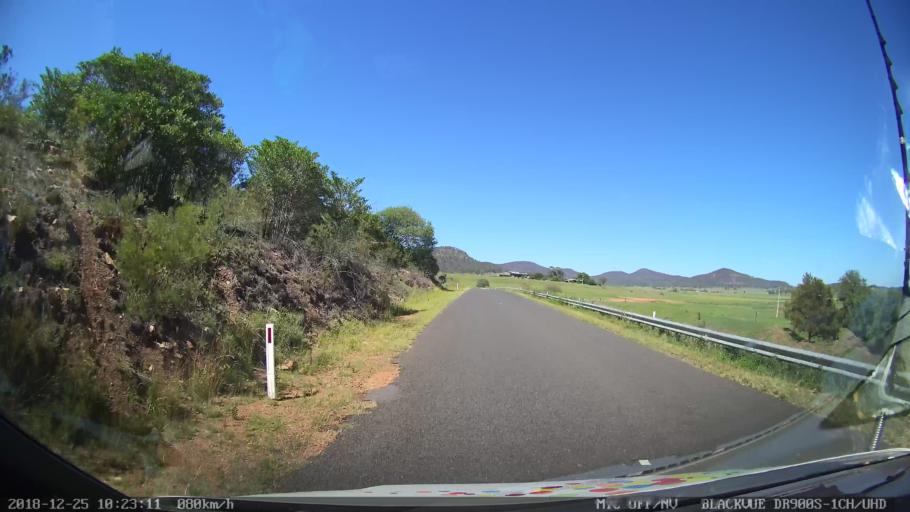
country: AU
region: New South Wales
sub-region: Muswellbrook
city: Denman
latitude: -32.3830
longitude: 150.5245
